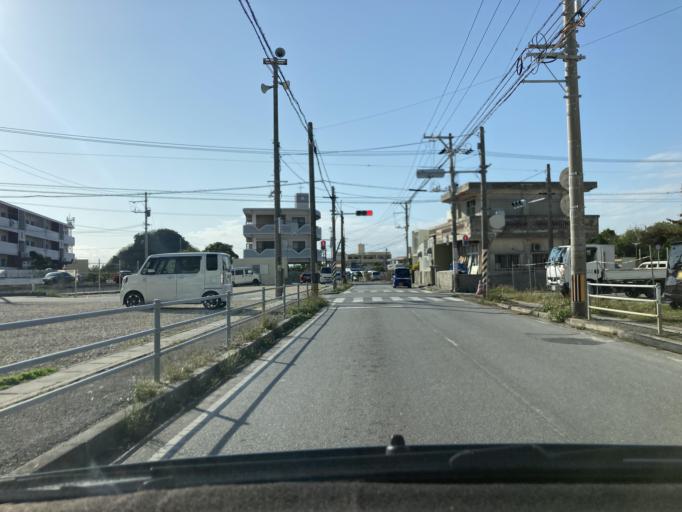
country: JP
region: Okinawa
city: Tomigusuku
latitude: 26.1647
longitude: 127.6659
